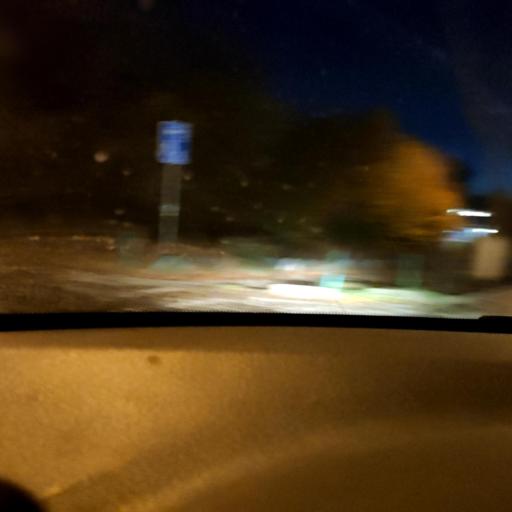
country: RU
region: Samara
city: Samara
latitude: 53.1878
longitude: 50.2047
